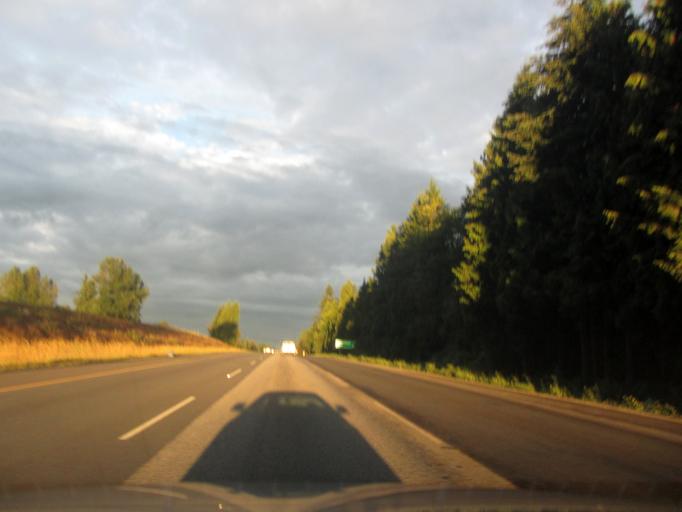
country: CA
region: British Columbia
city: Langley
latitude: 49.1285
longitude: -122.5620
